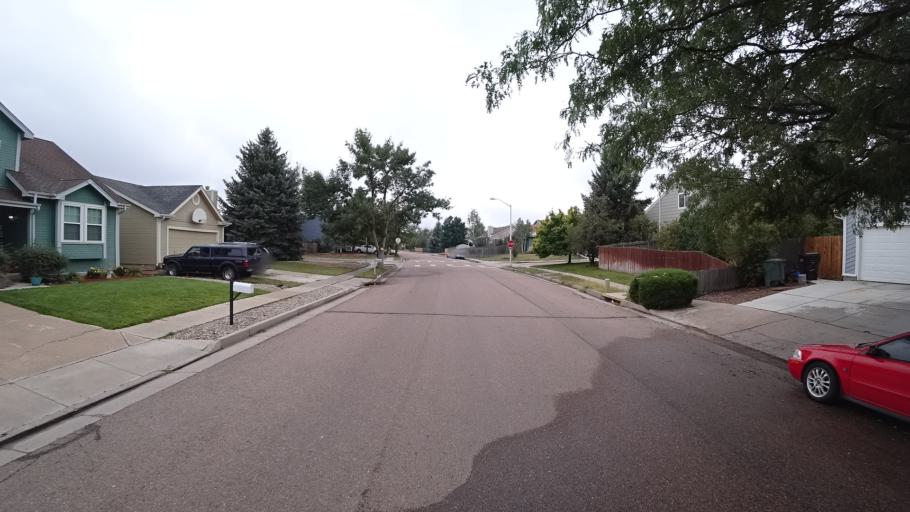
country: US
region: Colorado
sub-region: El Paso County
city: Cimarron Hills
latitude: 38.9212
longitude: -104.7546
